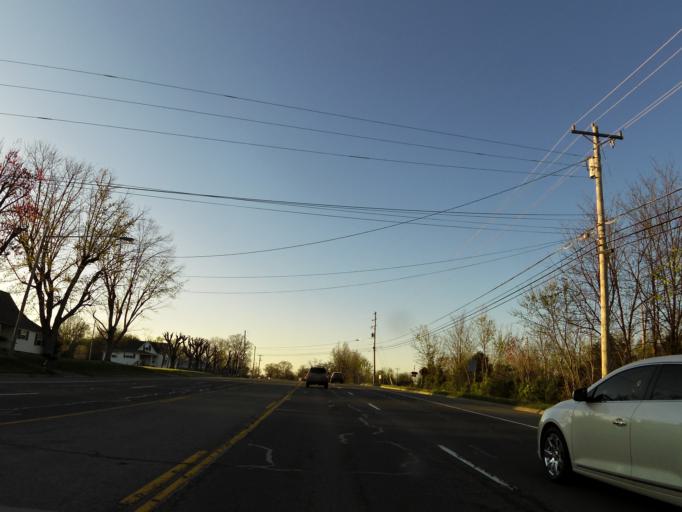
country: US
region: Tennessee
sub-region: Robertson County
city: Greenbrier
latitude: 36.4360
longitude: -86.8081
